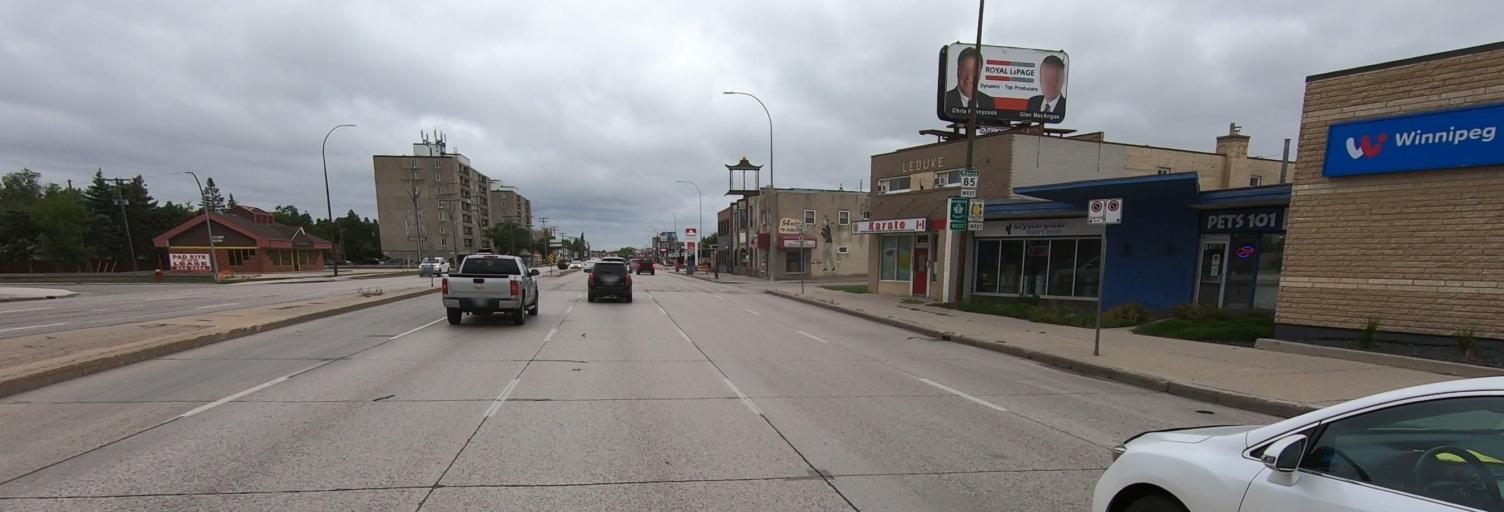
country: CA
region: Manitoba
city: Winnipeg
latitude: 49.8763
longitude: -97.2636
